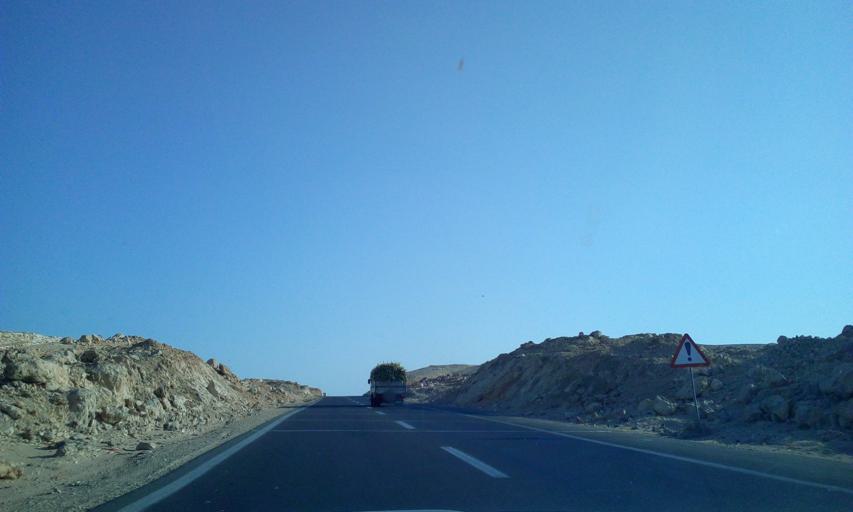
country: EG
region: As Suways
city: Ain Sukhna
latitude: 29.0458
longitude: 32.6188
